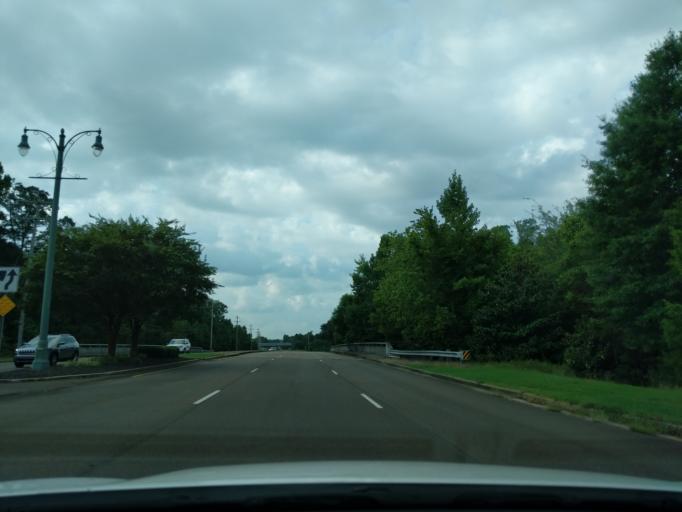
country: US
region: Tennessee
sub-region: Shelby County
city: Germantown
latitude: 35.0343
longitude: -89.7599
